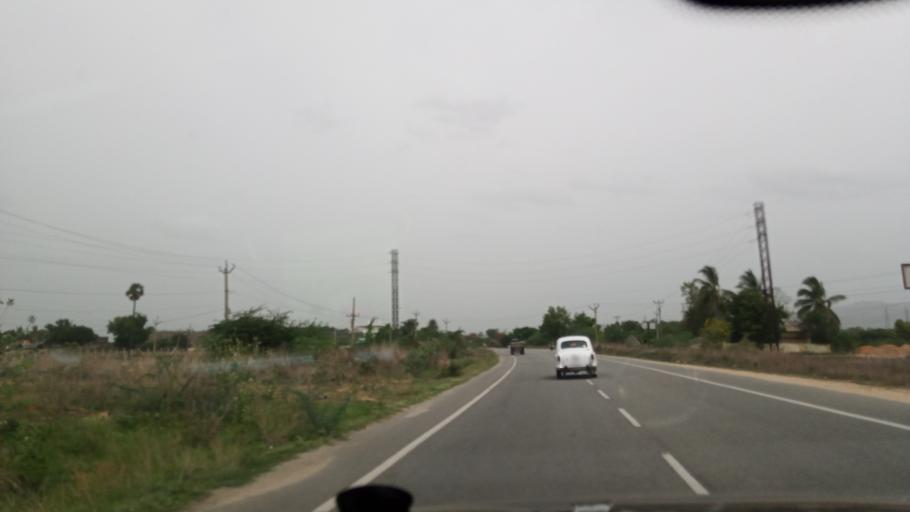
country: IN
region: Andhra Pradesh
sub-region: Chittoor
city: Nagari
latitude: 13.3535
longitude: 79.5744
